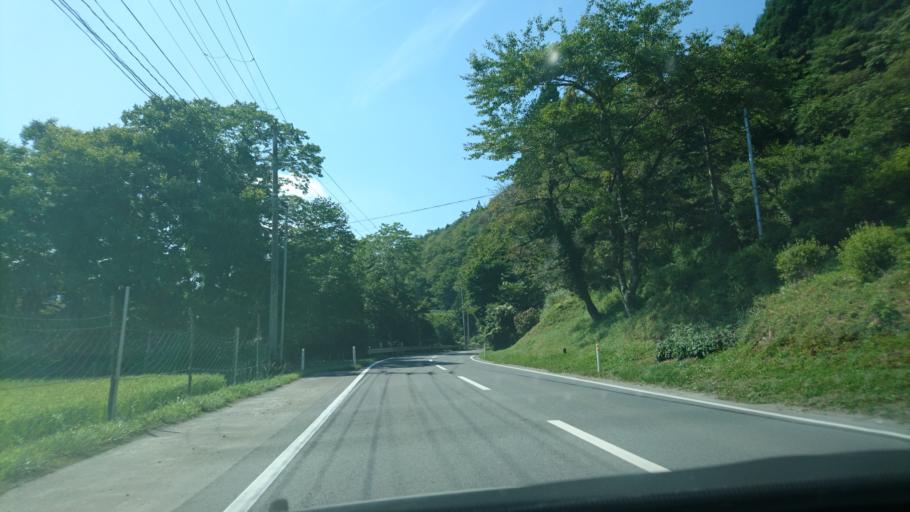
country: JP
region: Iwate
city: Ofunato
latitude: 39.0239
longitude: 141.5640
